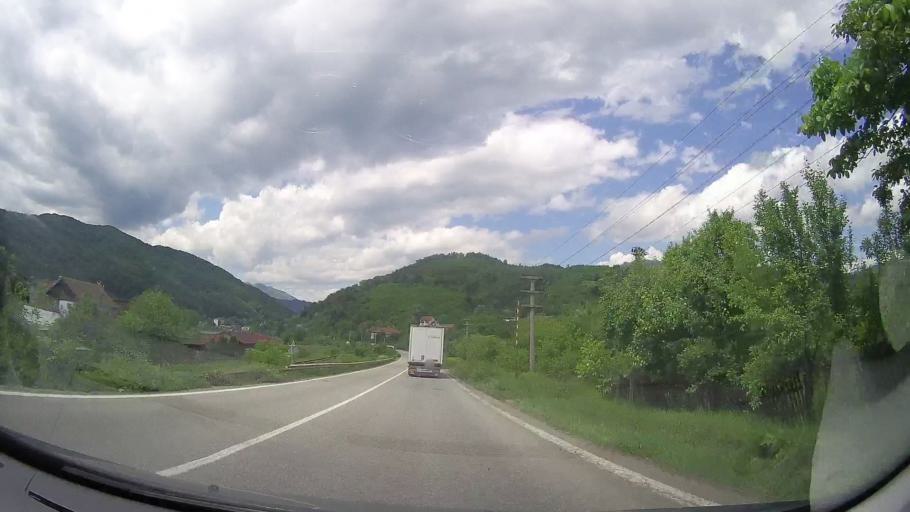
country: RO
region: Valcea
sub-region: Oras Calimanesti
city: Jiblea Veche
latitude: 45.2444
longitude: 24.3483
